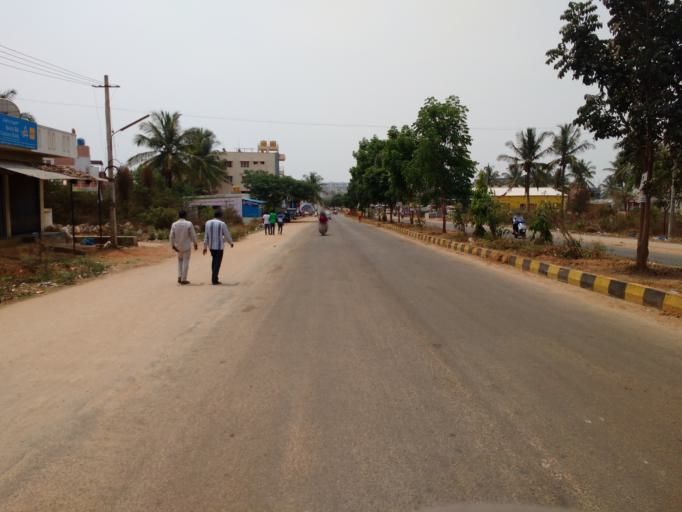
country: IN
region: Karnataka
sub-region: Hassan
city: Hassan
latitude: 13.0212
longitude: 76.1134
